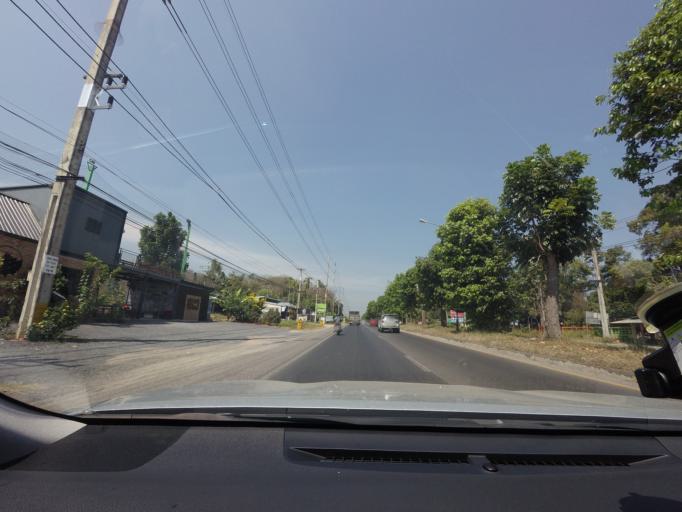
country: TH
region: Surat Thani
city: Kanchanadit
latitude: 9.1631
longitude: 99.4734
